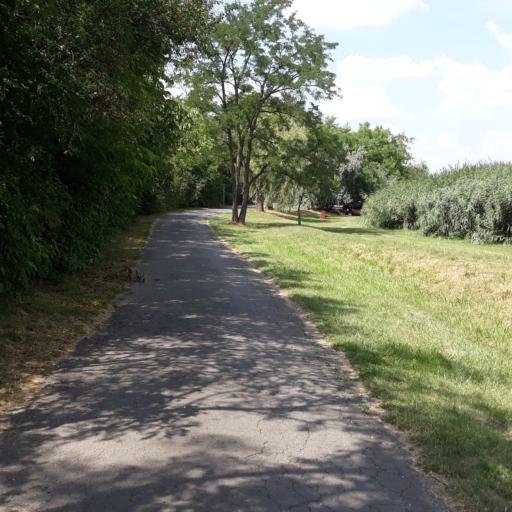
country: HU
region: Bekes
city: Oroshaza
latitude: 46.5614
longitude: 20.6247
